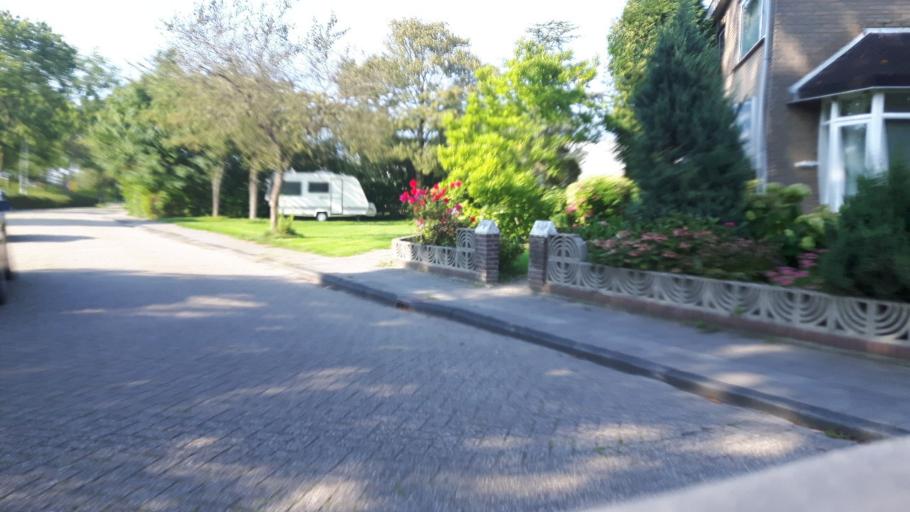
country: NL
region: Friesland
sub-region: Gemeente Franekeradeel
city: Franeker
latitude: 53.1901
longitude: 5.5551
